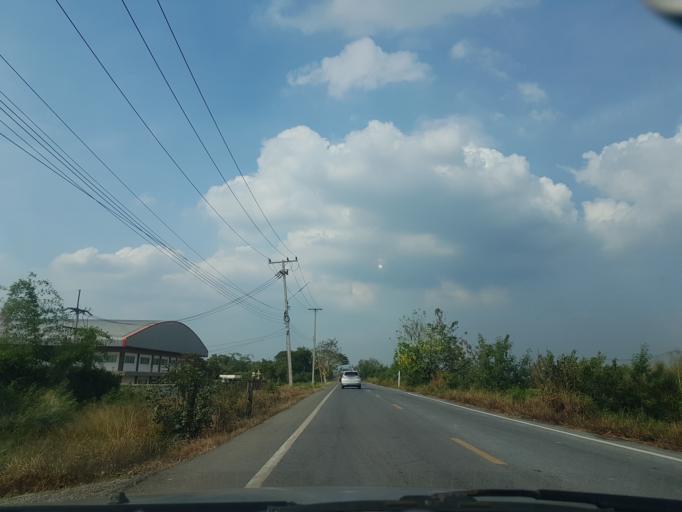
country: TH
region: Phra Nakhon Si Ayutthaya
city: Phachi
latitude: 14.4215
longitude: 100.7803
